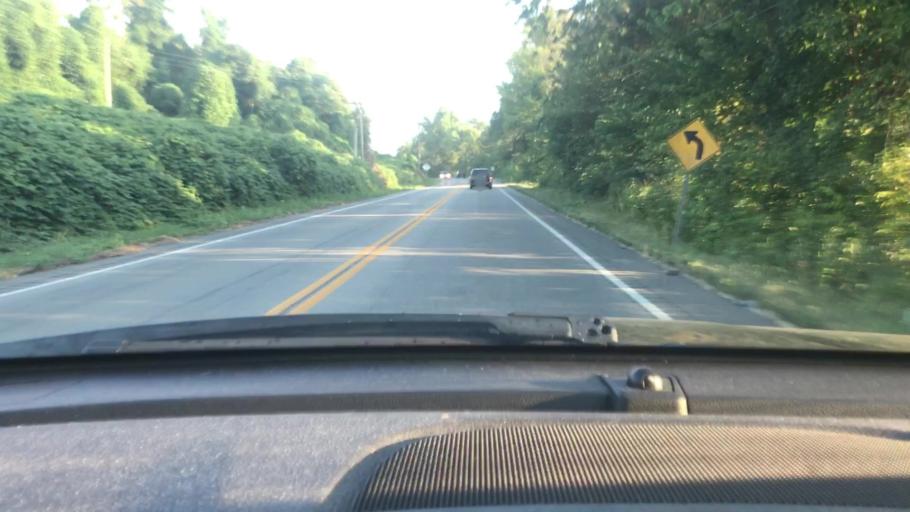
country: US
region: Tennessee
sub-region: Dickson County
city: Charlotte
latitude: 36.1574
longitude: -87.3560
